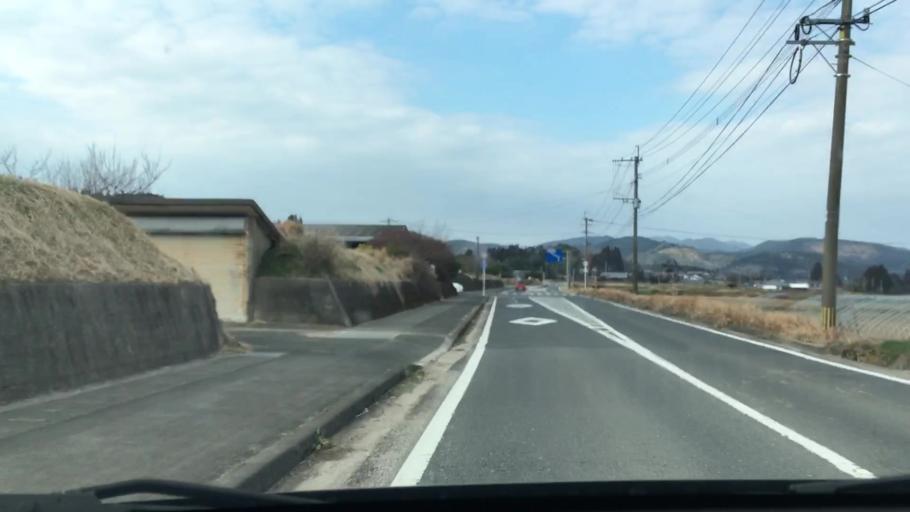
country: JP
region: Miyazaki
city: Kushima
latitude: 31.5179
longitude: 131.2385
